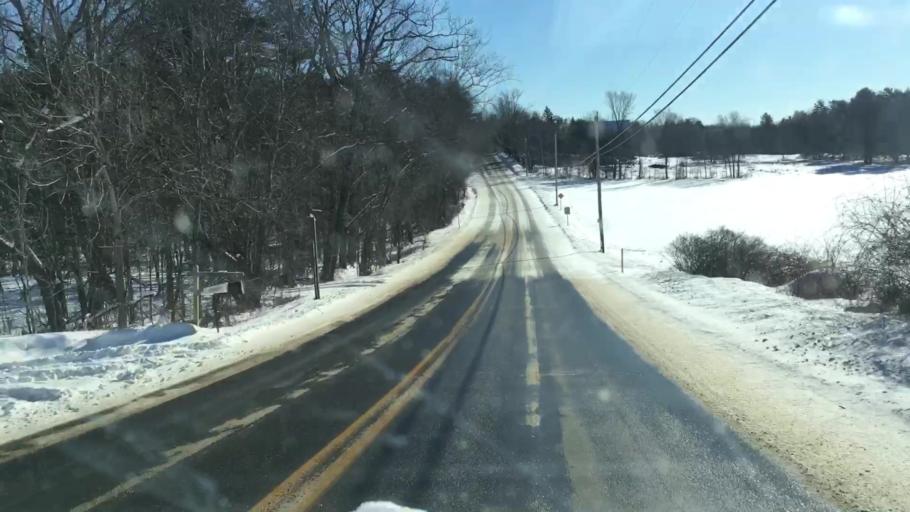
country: US
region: Maine
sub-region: Androscoggin County
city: Lisbon Falls
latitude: 43.9348
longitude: -70.0592
